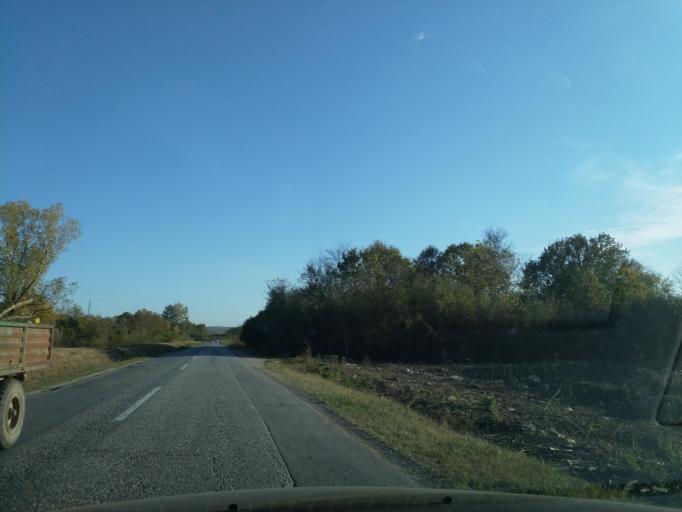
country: RS
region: Central Serbia
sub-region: Pomoravski Okrug
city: Svilajnac
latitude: 44.2263
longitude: 21.1470
